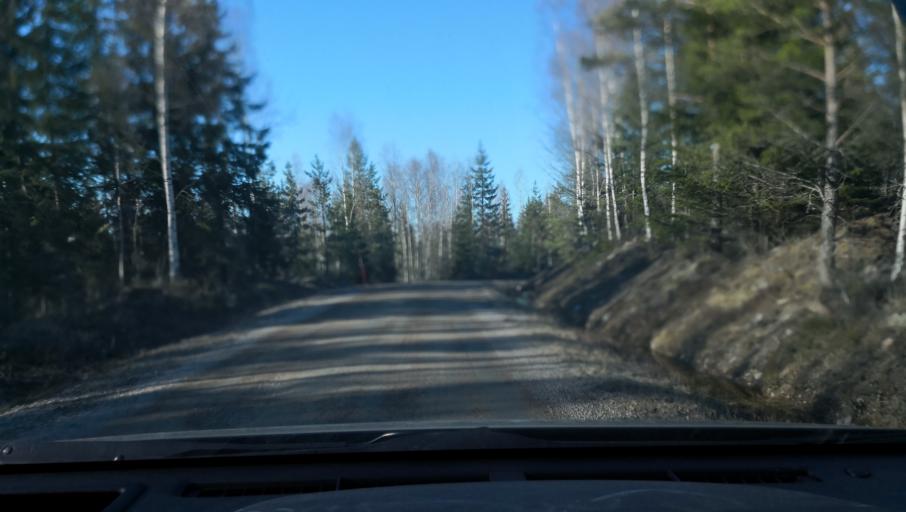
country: SE
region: Vaestmanland
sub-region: Sala Kommun
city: Sala
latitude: 60.1608
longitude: 16.6284
